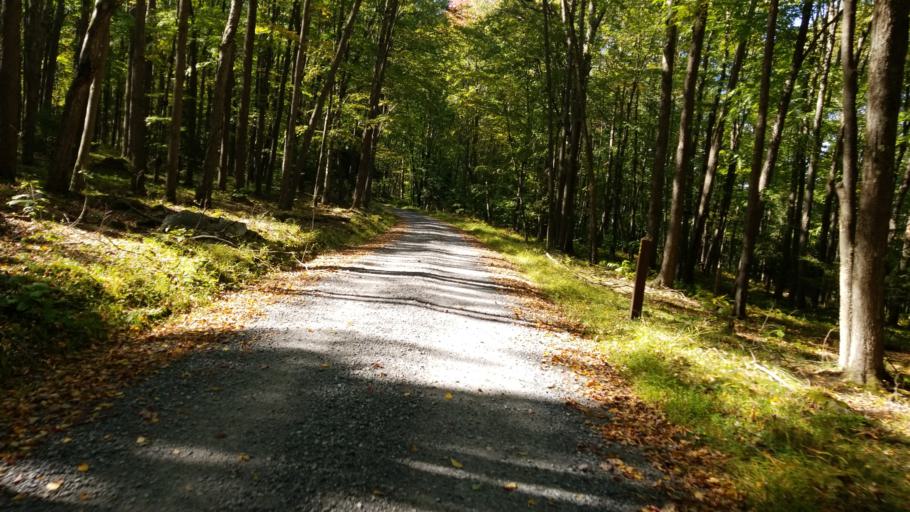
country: US
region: Pennsylvania
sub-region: Clearfield County
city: Clearfield
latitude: 41.1846
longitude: -78.5011
